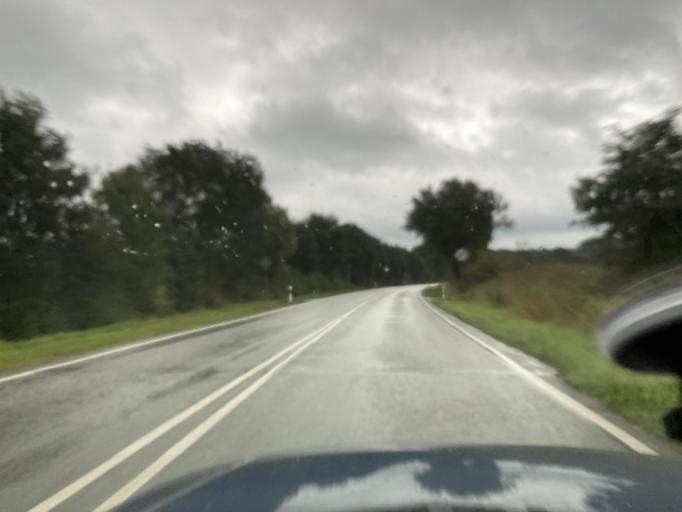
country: DE
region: Schleswig-Holstein
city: Suderdorf
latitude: 54.2195
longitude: 9.3486
